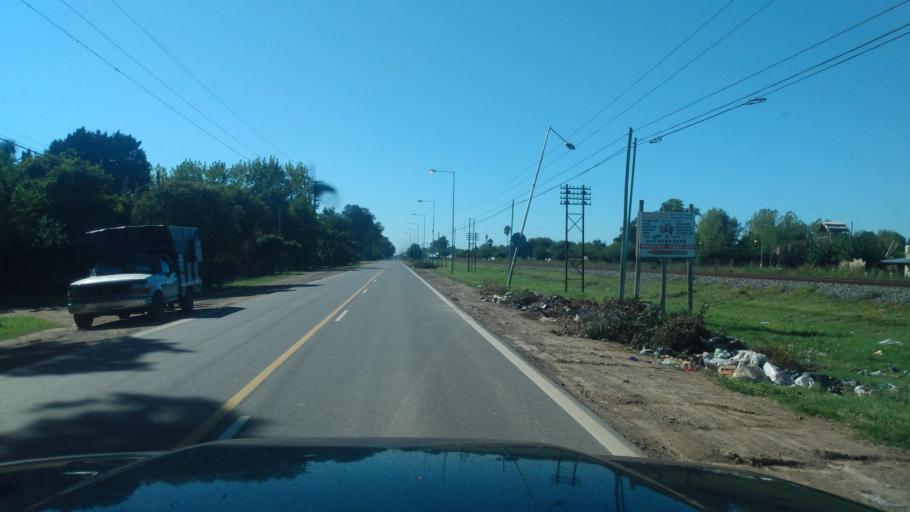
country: AR
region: Buenos Aires
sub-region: Partido de General Rodriguez
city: General Rodriguez
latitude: -34.5966
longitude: -59.0047
